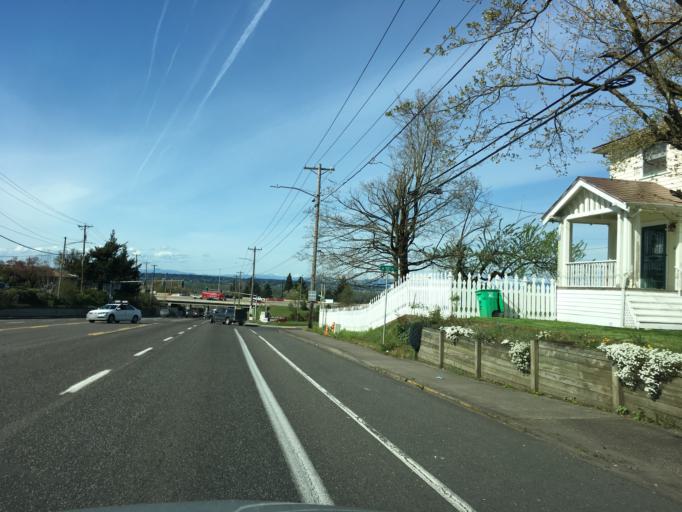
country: US
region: Oregon
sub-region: Multnomah County
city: Lents
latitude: 45.5439
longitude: -122.5374
